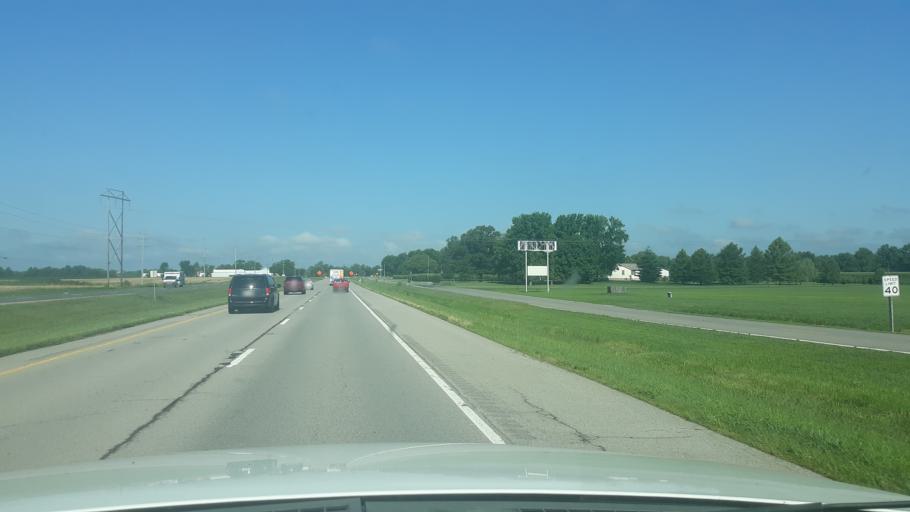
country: US
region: Illinois
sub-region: Williamson County
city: Marion
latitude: 37.7298
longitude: -88.8752
